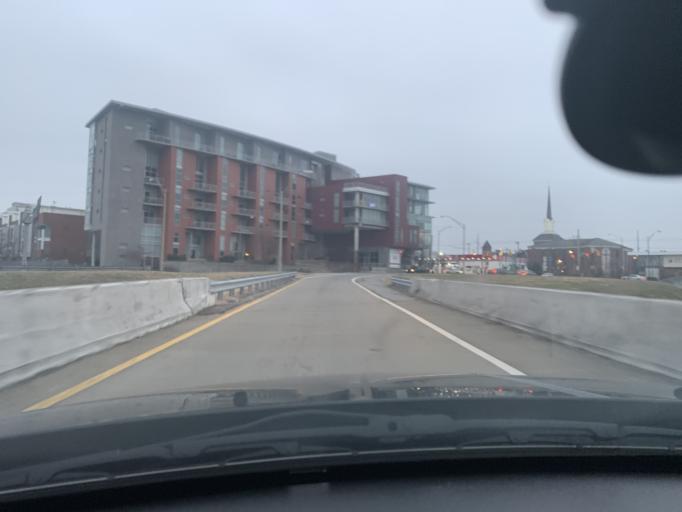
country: US
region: Tennessee
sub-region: Davidson County
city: Nashville
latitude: 36.1736
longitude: -86.7665
